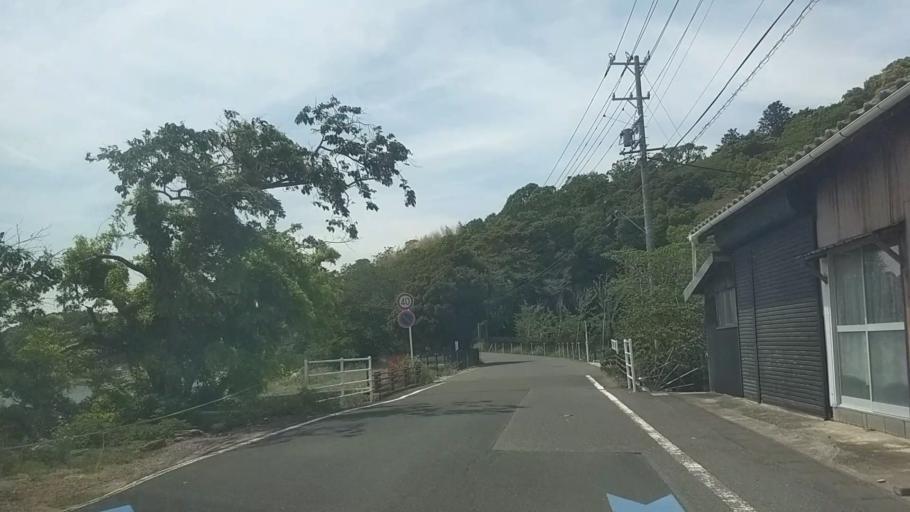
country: JP
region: Shizuoka
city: Kosai-shi
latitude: 34.7855
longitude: 137.5867
